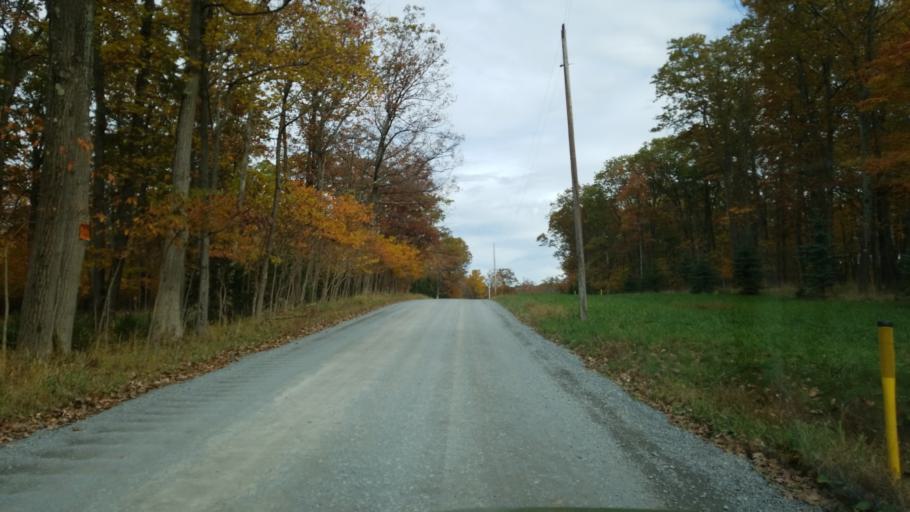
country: US
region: Pennsylvania
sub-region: Clearfield County
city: Clearfield
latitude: 41.1581
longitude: -78.4569
